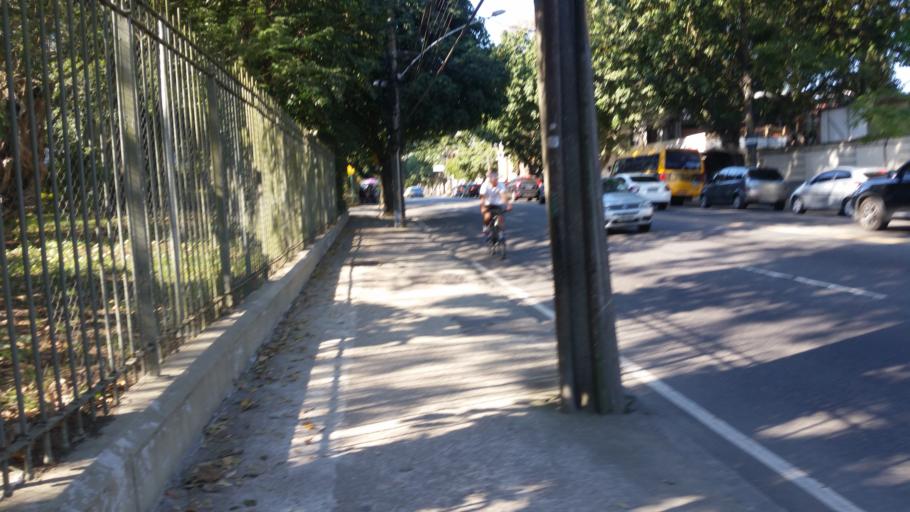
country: BR
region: Rio de Janeiro
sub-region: Rio De Janeiro
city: Rio de Janeiro
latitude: -22.9715
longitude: -43.2237
